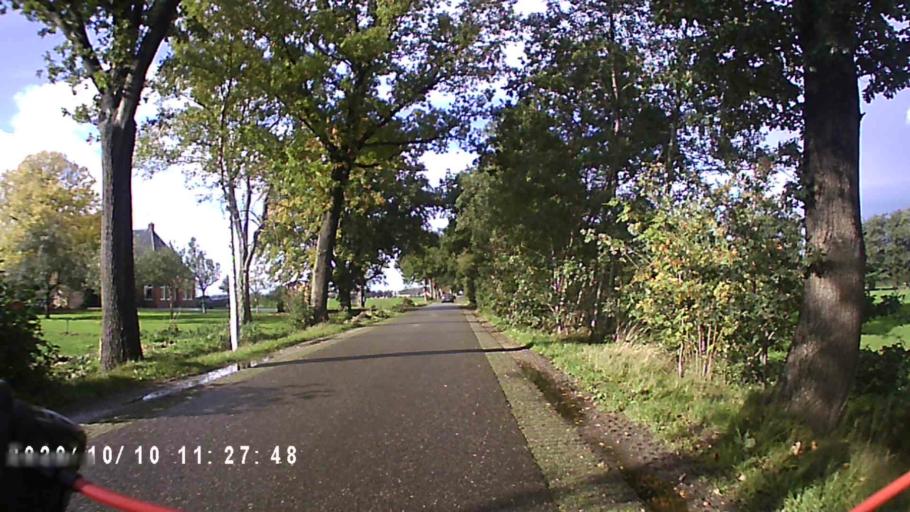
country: NL
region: Friesland
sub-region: Gemeente Smallingerland
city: Drachtstercompagnie
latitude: 53.0874
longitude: 6.1565
